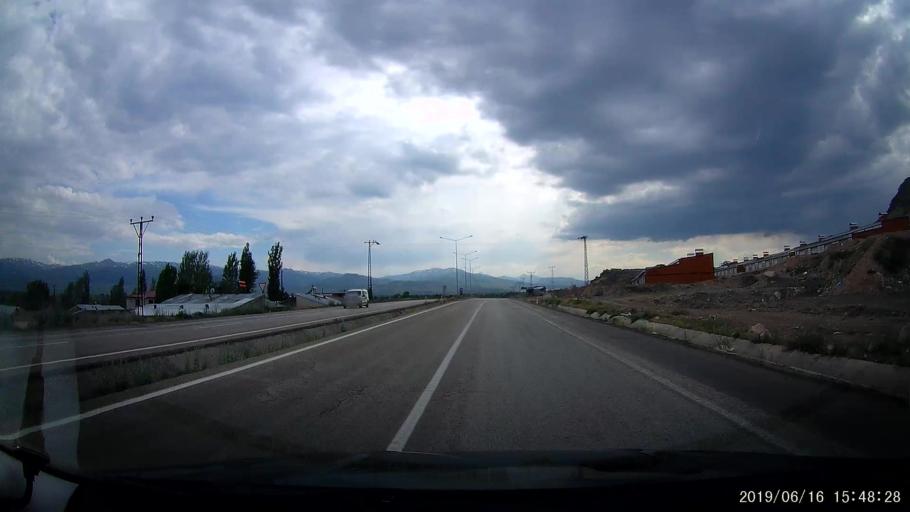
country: TR
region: Erzurum
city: Pasinler
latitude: 39.9827
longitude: 41.7006
